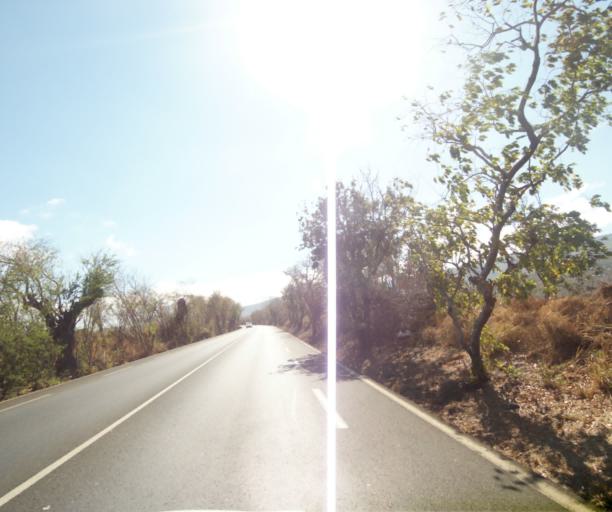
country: RE
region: Reunion
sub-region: Reunion
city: Saint-Paul
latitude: -20.9843
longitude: 55.3009
